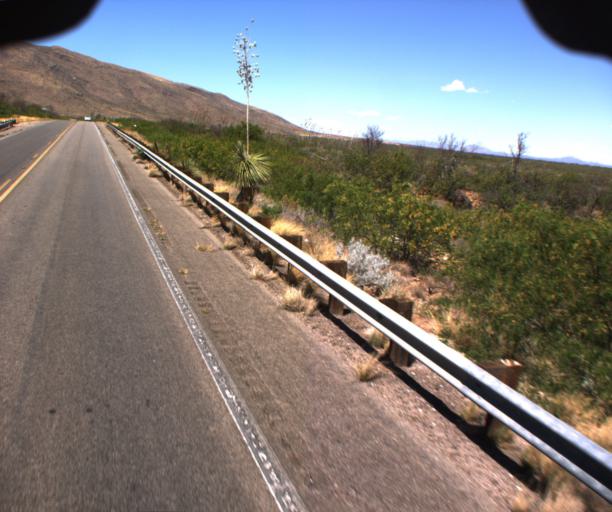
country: US
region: Arizona
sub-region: Cochise County
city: Bisbee
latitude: 31.4327
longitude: -109.8126
